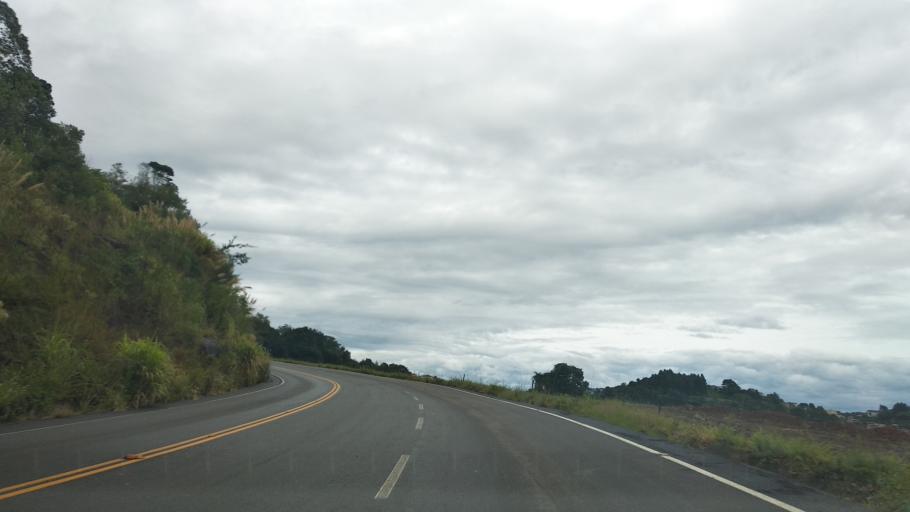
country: BR
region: Santa Catarina
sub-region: Videira
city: Videira
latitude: -27.0041
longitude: -51.1735
